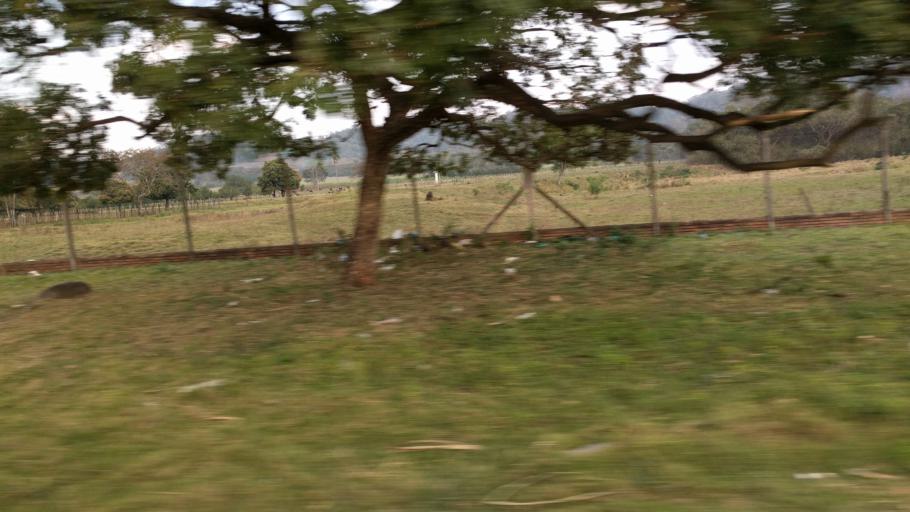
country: BO
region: Santa Cruz
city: Jorochito
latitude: -18.1049
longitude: -63.4560
